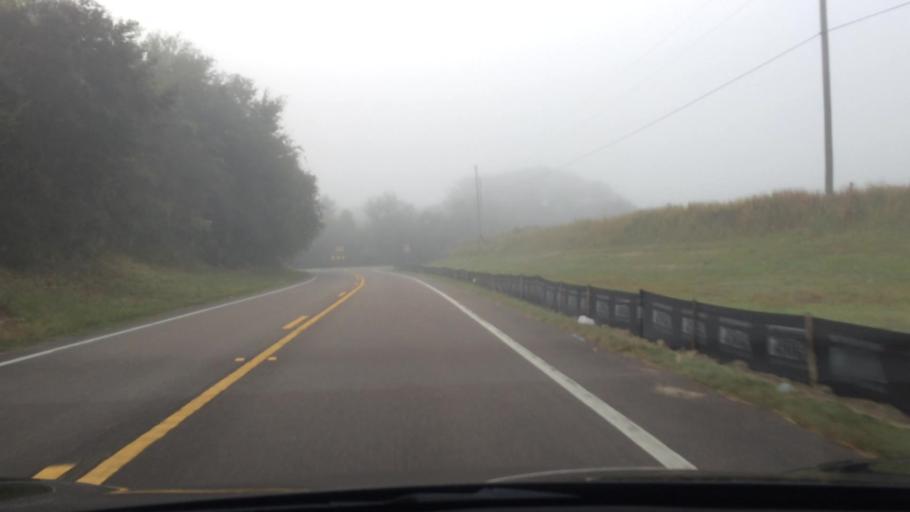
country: US
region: Florida
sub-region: Hillsborough County
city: Lutz
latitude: 28.1725
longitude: -82.4034
